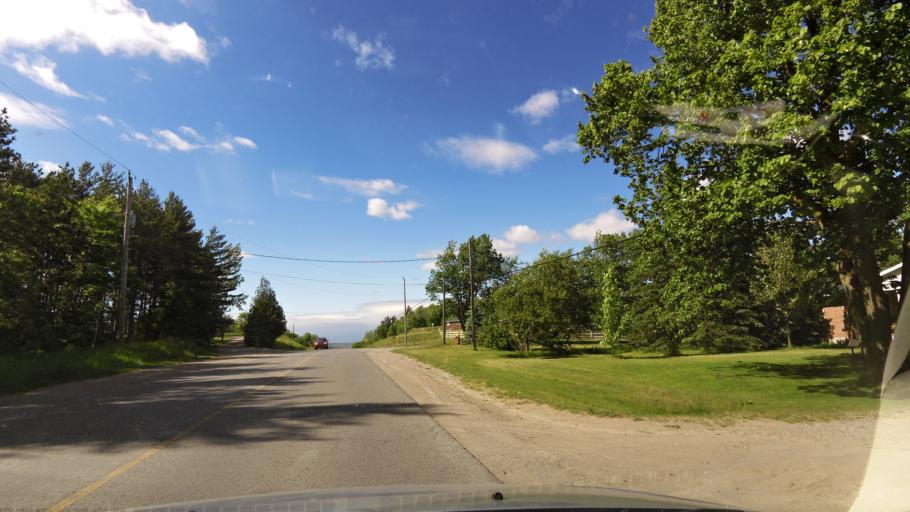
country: CA
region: Ontario
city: Bradford West Gwillimbury
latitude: 44.1636
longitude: -79.6159
